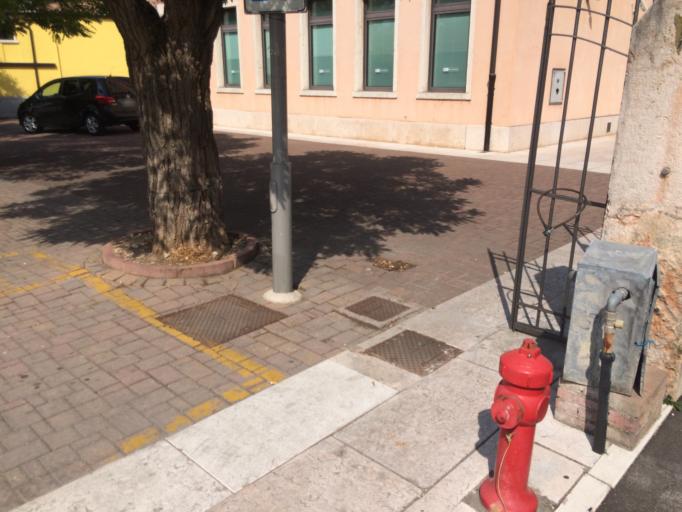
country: IT
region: Veneto
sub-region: Provincia di Verona
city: Volargne
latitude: 45.5217
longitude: 10.8064
